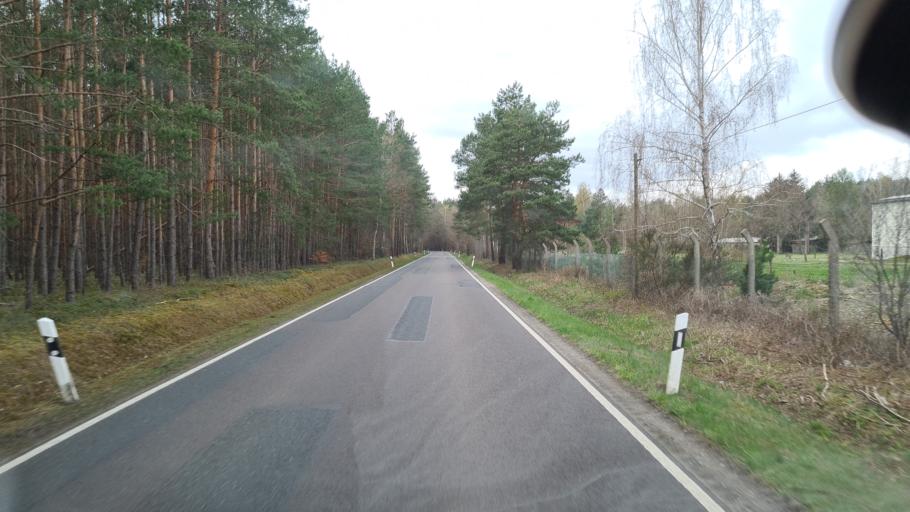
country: DE
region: Brandenburg
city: Schwarzbach
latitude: 51.4496
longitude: 13.9569
